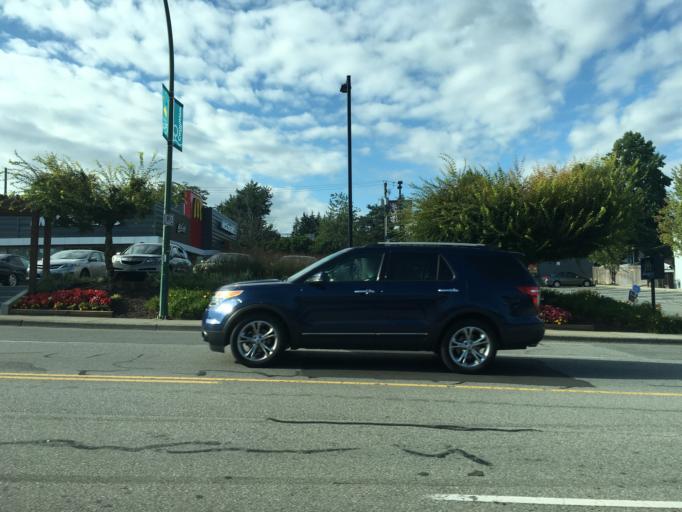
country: CA
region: British Columbia
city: Port Moody
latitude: 49.2489
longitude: -122.8600
